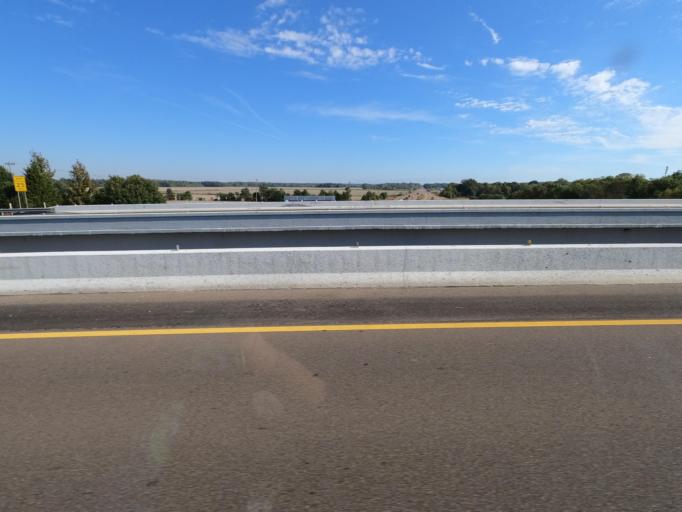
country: US
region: Tennessee
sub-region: Shelby County
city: Arlington
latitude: 35.2890
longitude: -89.6867
